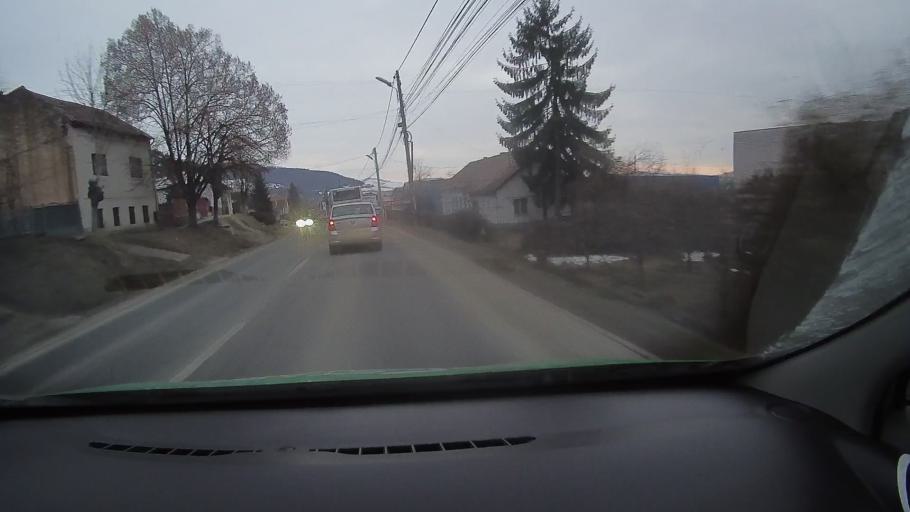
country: RO
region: Harghita
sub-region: Municipiul Odorheiu Secuiesc
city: Odorheiu Secuiesc
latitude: 46.2924
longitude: 25.2898
